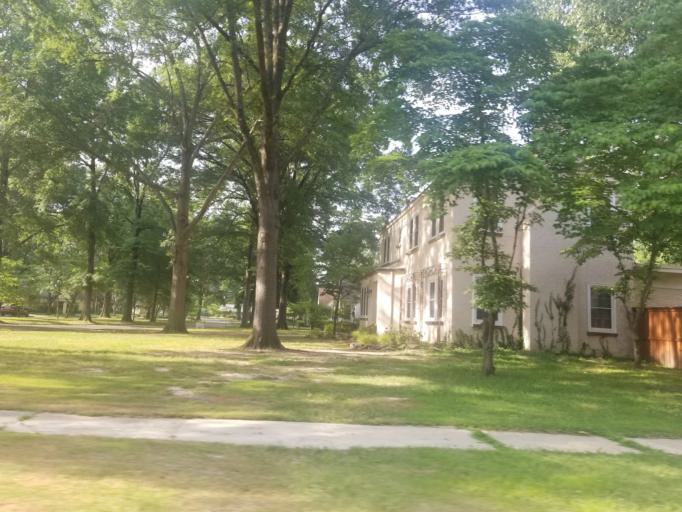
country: US
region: Arkansas
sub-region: Cross County
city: Wynne
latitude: 35.2254
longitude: -90.7823
